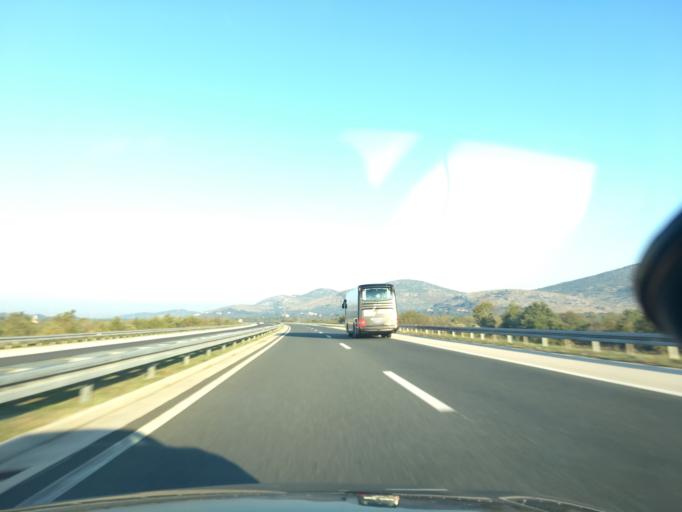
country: HR
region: Sibensko-Kniniska
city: Drnis
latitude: 43.6756
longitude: 16.1543
